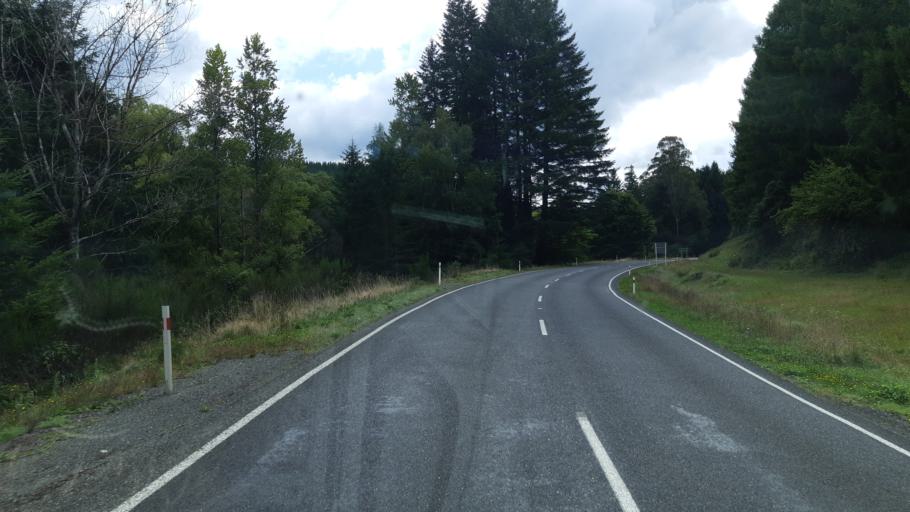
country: NZ
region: Tasman
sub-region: Tasman District
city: Wakefield
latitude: -41.6030
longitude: 172.7587
